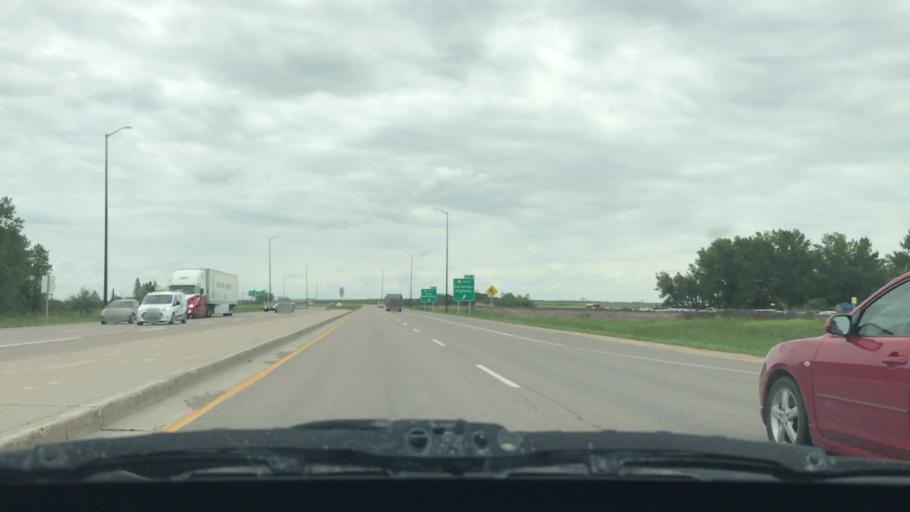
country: CA
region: Manitoba
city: Winnipeg
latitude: 49.8386
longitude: -96.9804
